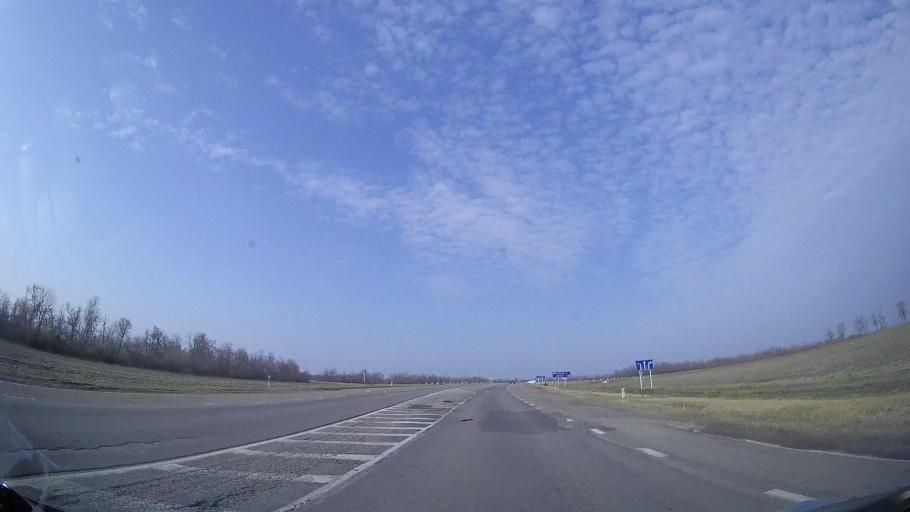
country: RU
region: Rostov
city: Tselina
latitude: 46.5109
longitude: 41.0113
